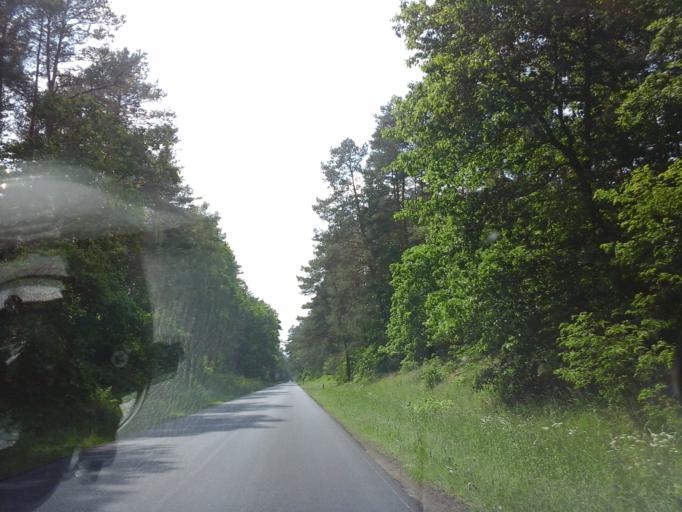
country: PL
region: West Pomeranian Voivodeship
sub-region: Powiat choszczenski
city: Drawno
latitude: 53.2064
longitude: 15.7163
